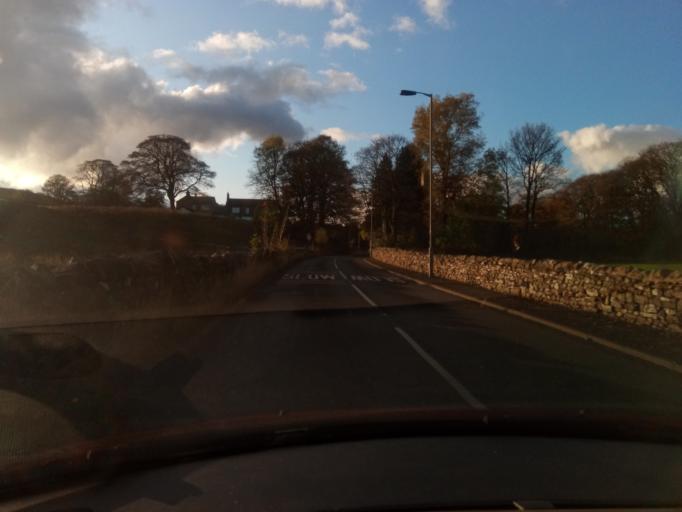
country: GB
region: England
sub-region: County Durham
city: Newbiggin
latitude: 54.7409
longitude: -2.1960
